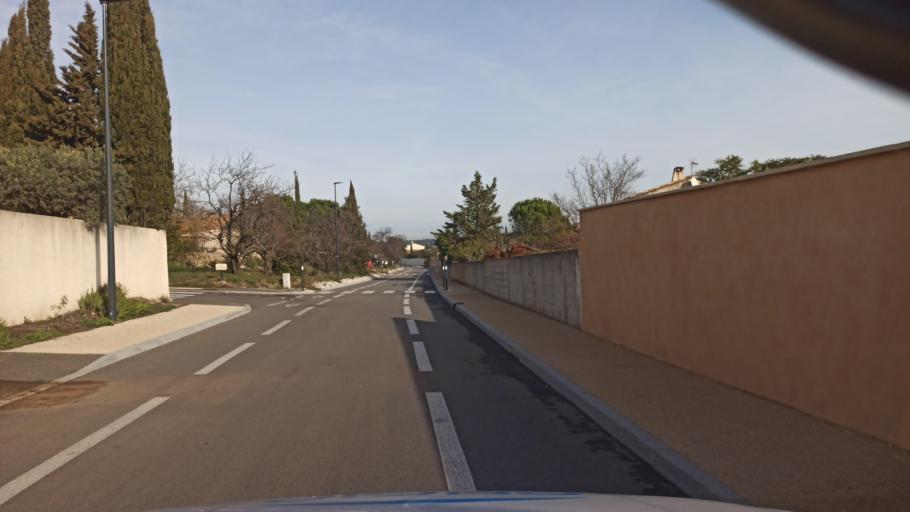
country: FR
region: Languedoc-Roussillon
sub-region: Departement du Gard
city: Villeneuve-les-Avignon
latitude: 43.9766
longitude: 4.7816
